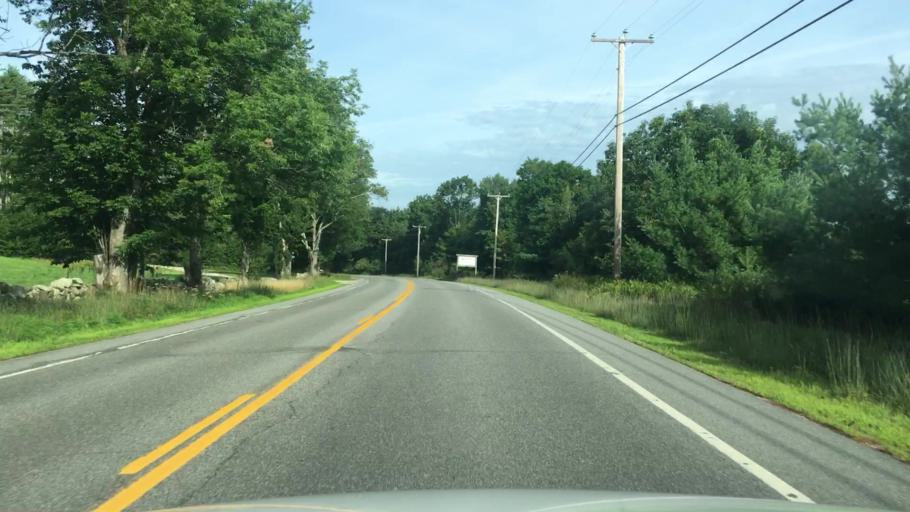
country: US
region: Maine
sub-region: York County
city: Cornish
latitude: 43.8049
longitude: -70.8341
